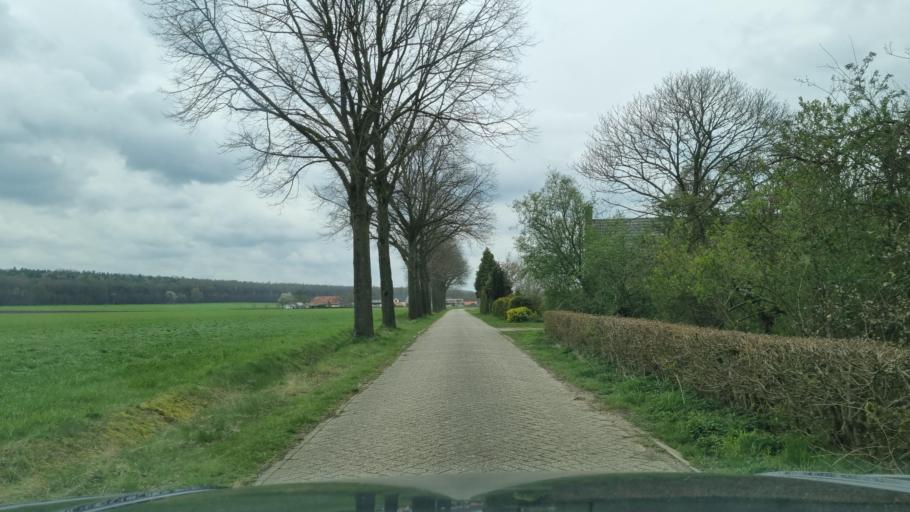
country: NL
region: Gelderland
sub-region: Gemeente Groesbeek
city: De Horst
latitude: 51.7689
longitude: 5.9821
